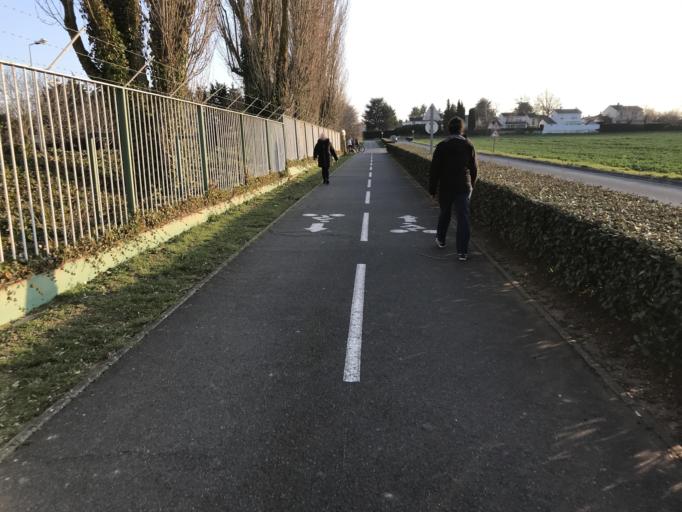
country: FR
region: Ile-de-France
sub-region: Departement de l'Essonne
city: Nozay
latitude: 48.6659
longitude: 2.2357
